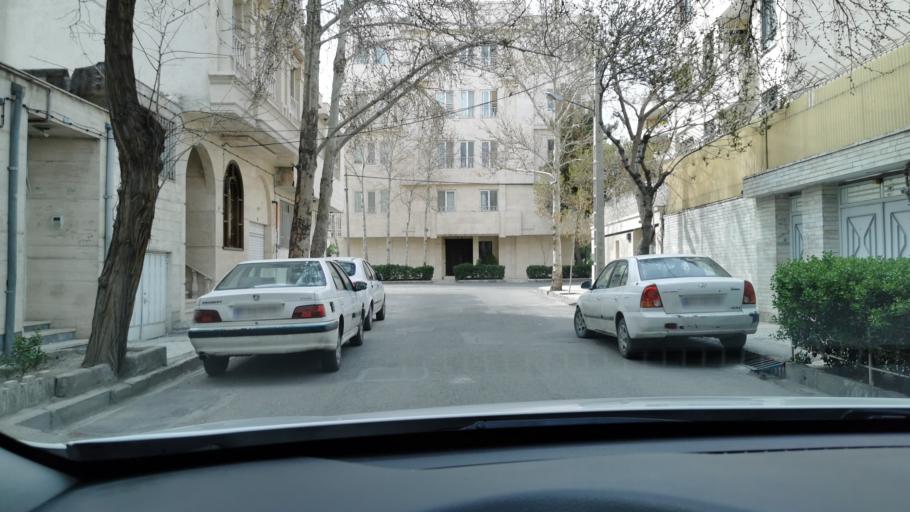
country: IR
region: Razavi Khorasan
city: Mashhad
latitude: 36.2917
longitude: 59.5762
